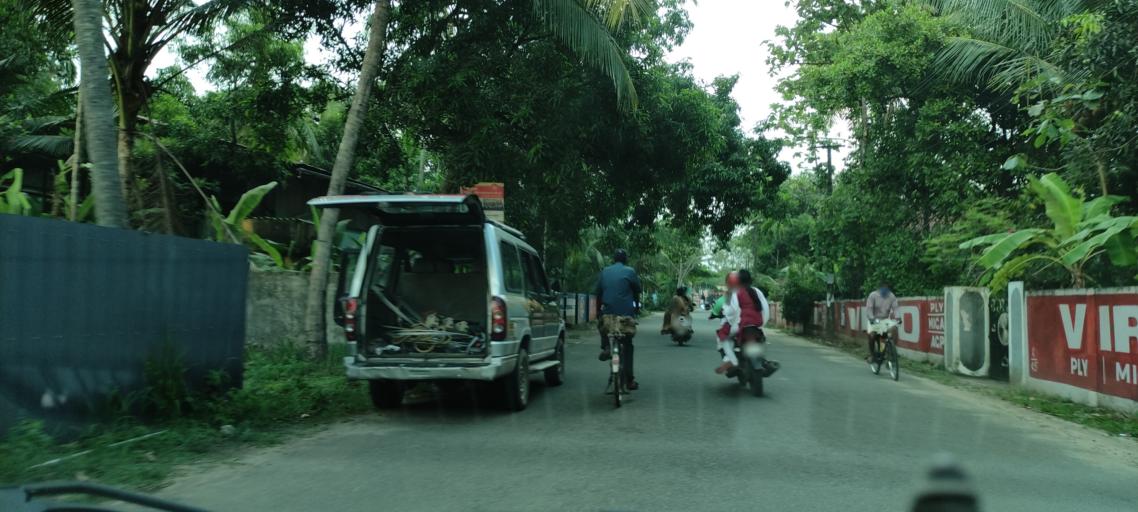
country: IN
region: Kerala
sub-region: Alappuzha
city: Kutiatodu
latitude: 9.8204
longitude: 76.3483
